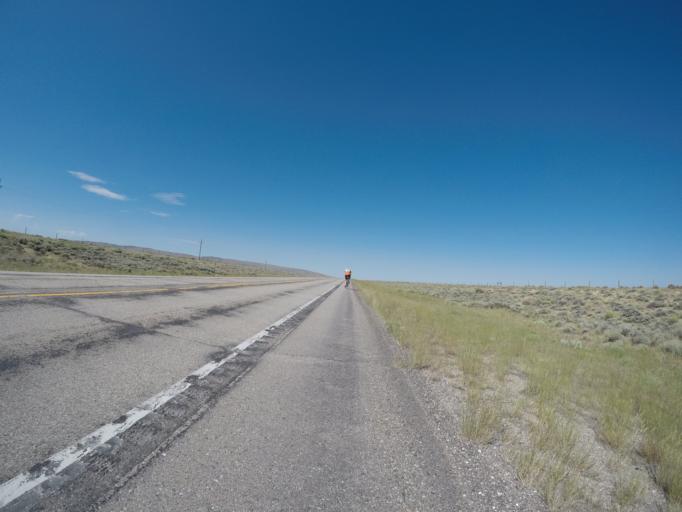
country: US
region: Wyoming
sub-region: Carbon County
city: Saratoga
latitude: 41.8178
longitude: -106.6627
